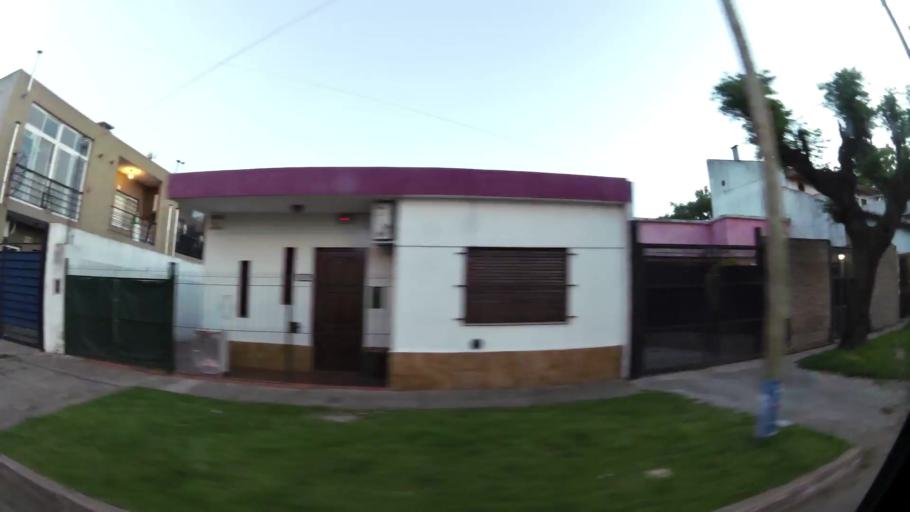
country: AR
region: Buenos Aires
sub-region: Partido de Quilmes
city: Quilmes
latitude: -34.7730
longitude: -58.2069
